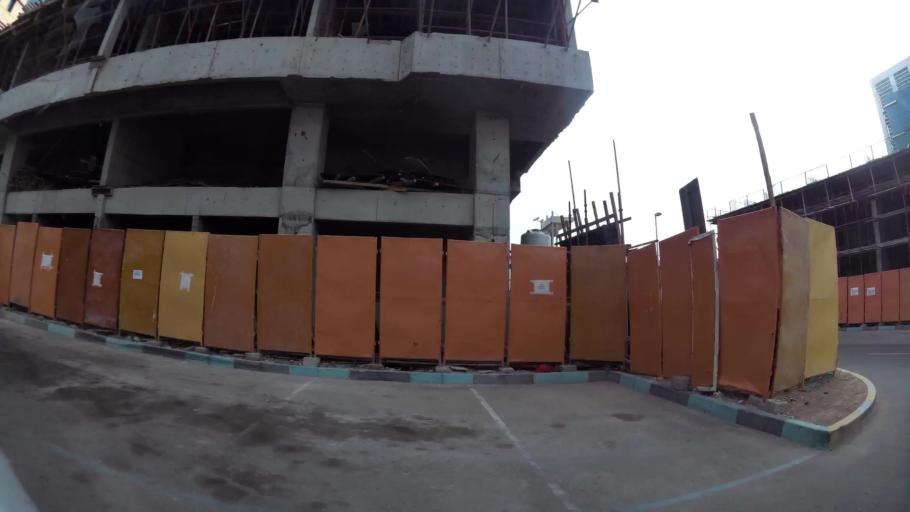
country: AE
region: Abu Dhabi
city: Abu Dhabi
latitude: 24.4723
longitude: 54.3788
